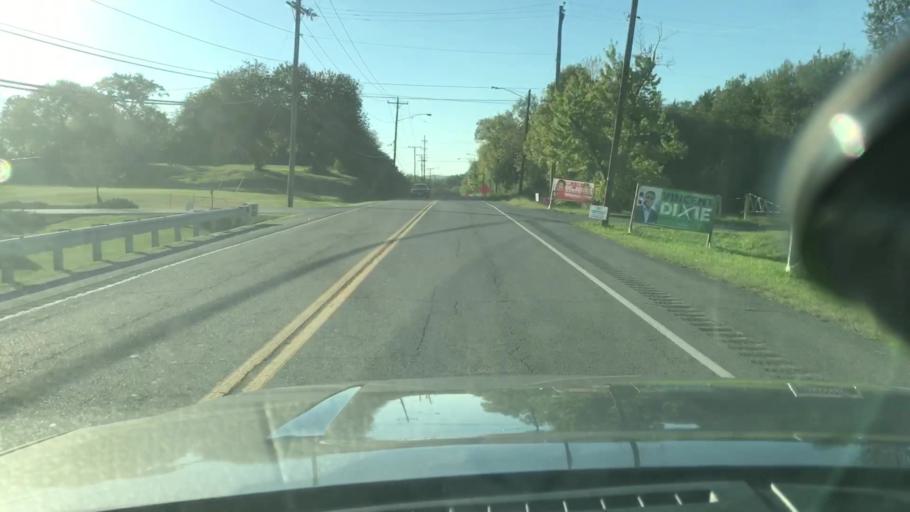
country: US
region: Tennessee
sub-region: Davidson County
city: Nashville
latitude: 36.1980
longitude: -86.8397
